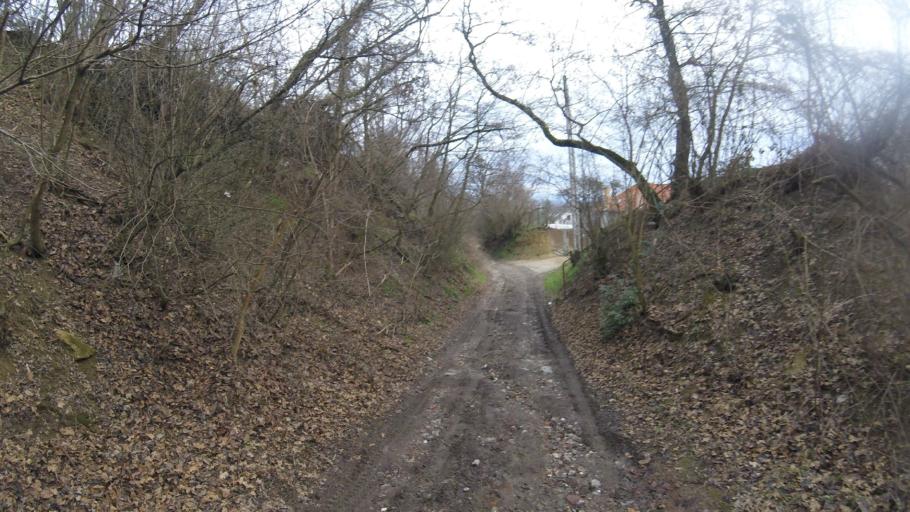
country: HU
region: Pest
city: Nagykovacsi
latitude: 47.6657
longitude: 19.0142
